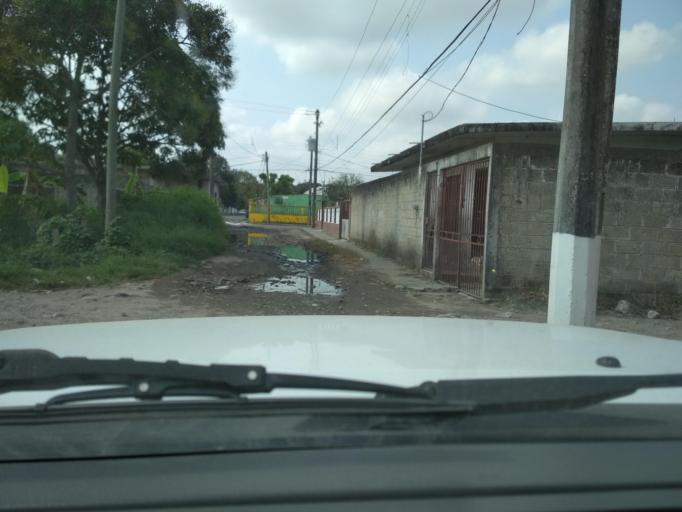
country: MX
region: Veracruz
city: El Tejar
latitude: 19.0793
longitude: -96.1622
